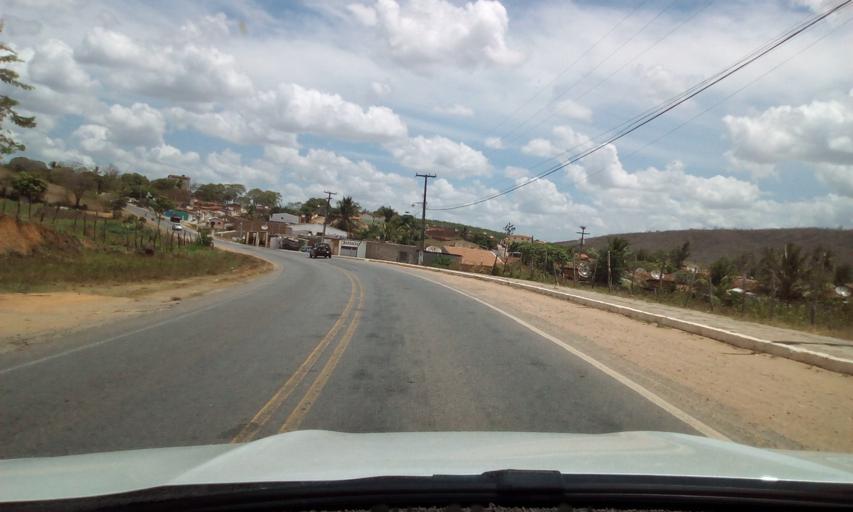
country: BR
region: Paraiba
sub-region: Guarabira
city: Guarabira
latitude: -6.8973
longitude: -35.5160
